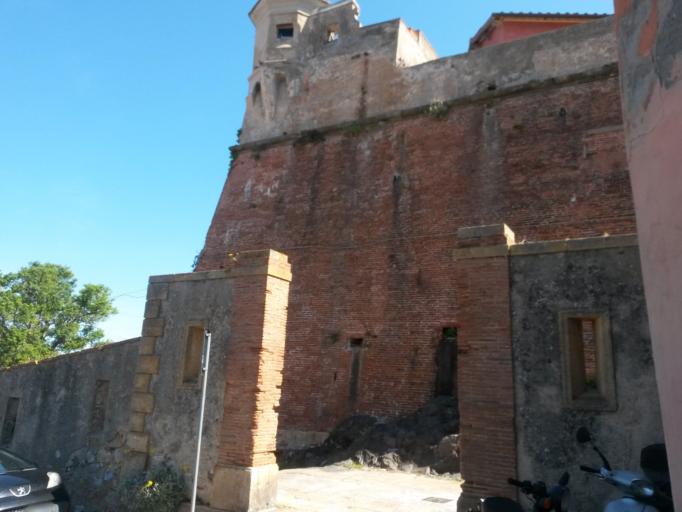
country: IT
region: Tuscany
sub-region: Provincia di Livorno
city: Portoferraio
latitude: 42.8158
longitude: 10.3332
